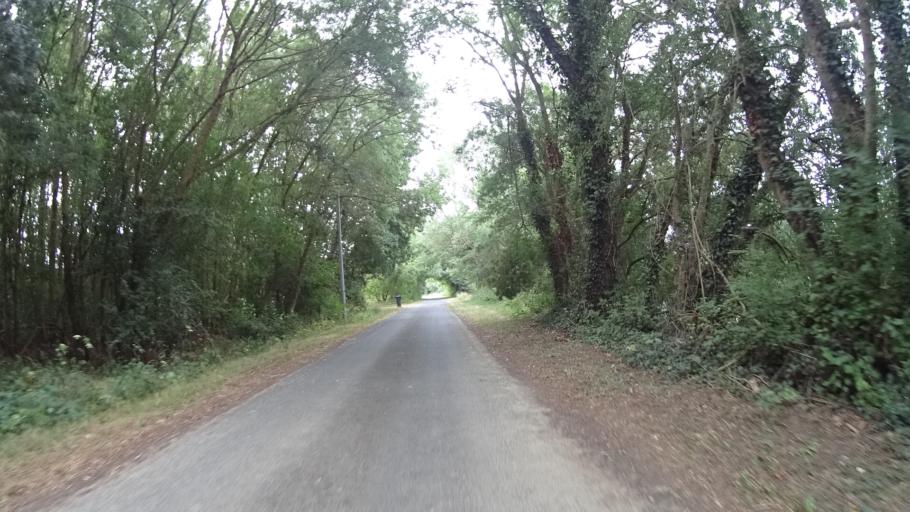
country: FR
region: Pays de la Loire
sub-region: Departement de Maine-et-Loire
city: Montjean-sur-Loire
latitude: 47.3803
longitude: -0.8301
